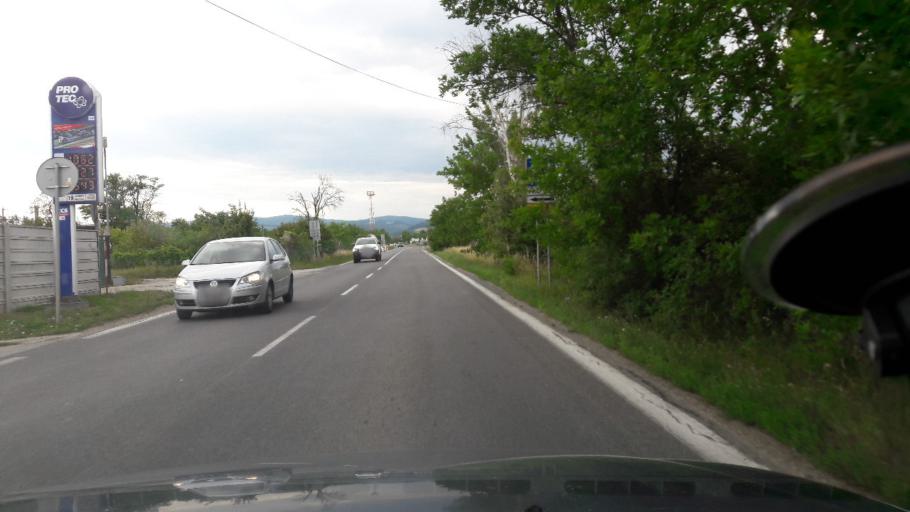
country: SK
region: Bratislavsky
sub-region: Okres Pezinok
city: Pezinok
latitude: 48.2841
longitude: 17.2866
